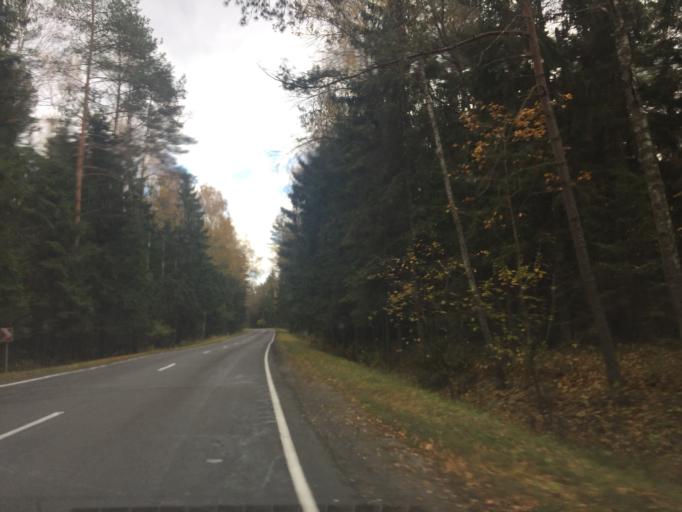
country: BY
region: Minsk
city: Svir
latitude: 54.9238
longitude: 26.5061
